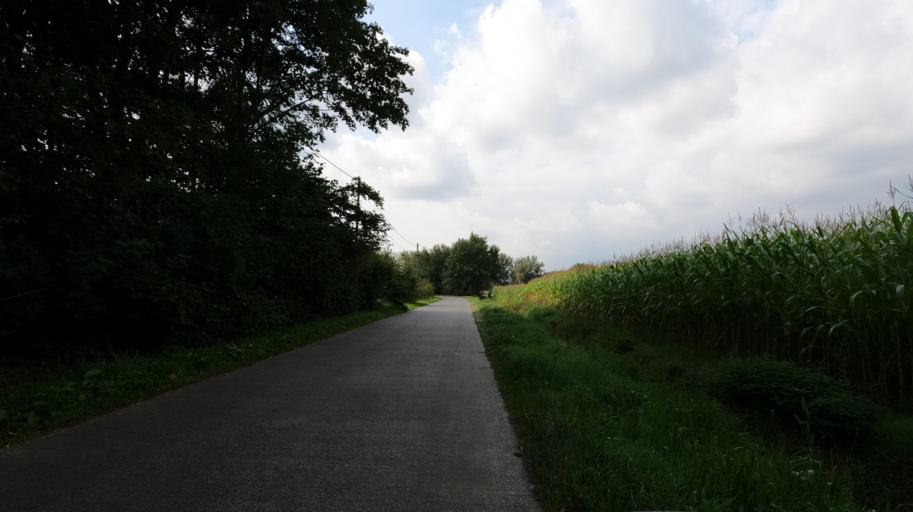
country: BE
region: Flanders
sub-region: Provincie Antwerpen
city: Sint-Katelijne-Waver
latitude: 51.0800
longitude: 4.5592
